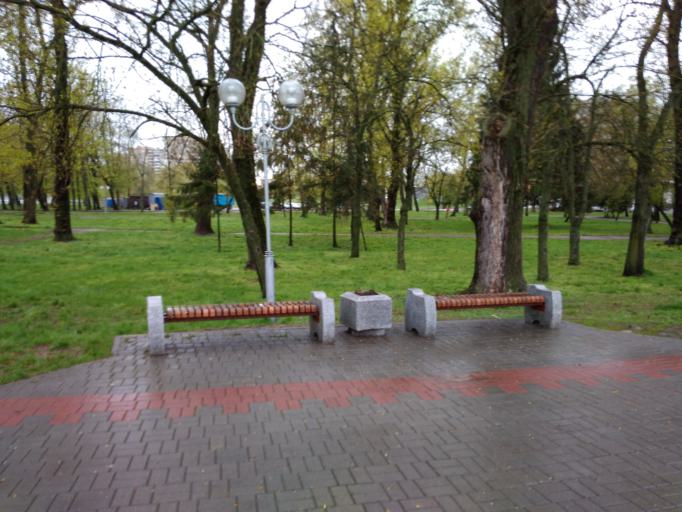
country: BY
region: Brest
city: Brest
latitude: 52.0820
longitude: 23.6998
